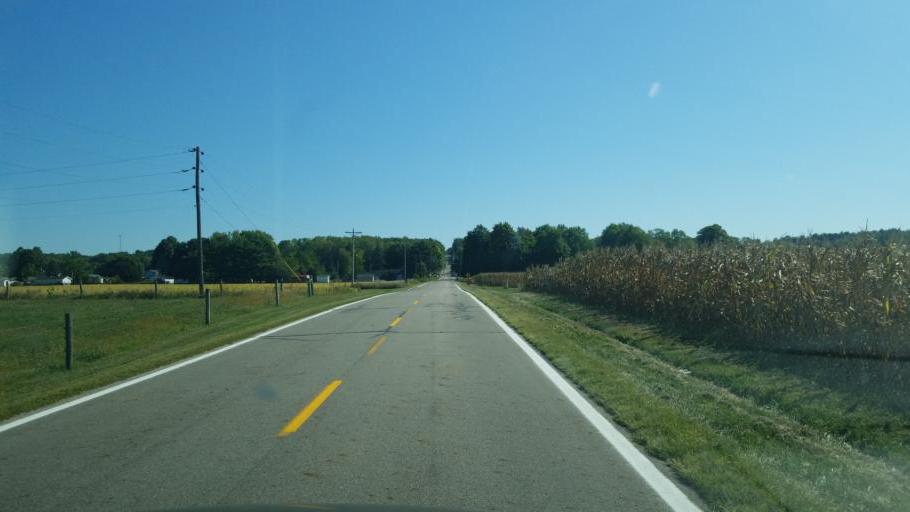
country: US
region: Ohio
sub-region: Champaign County
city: North Lewisburg
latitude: 40.2121
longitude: -83.6387
